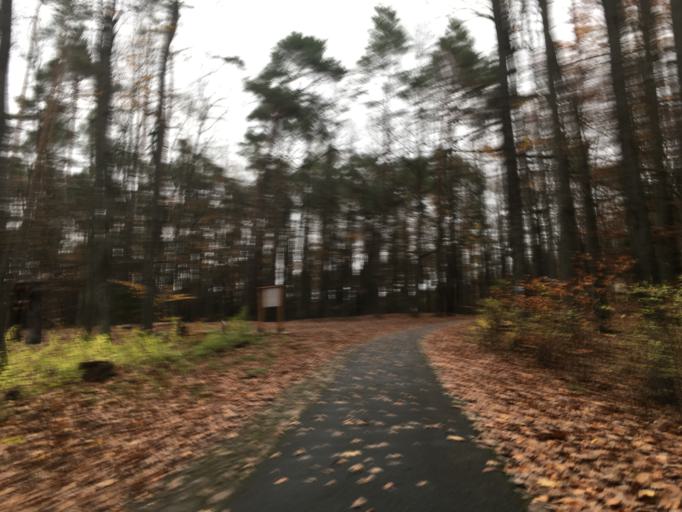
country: DE
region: Brandenburg
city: Mixdorf
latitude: 52.1656
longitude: 14.4421
